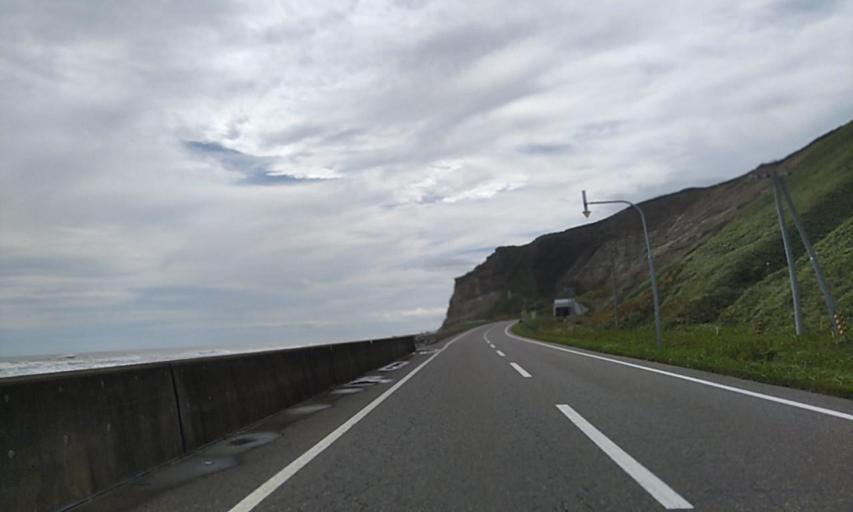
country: JP
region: Hokkaido
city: Obihiro
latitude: 42.7666
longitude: 143.7674
